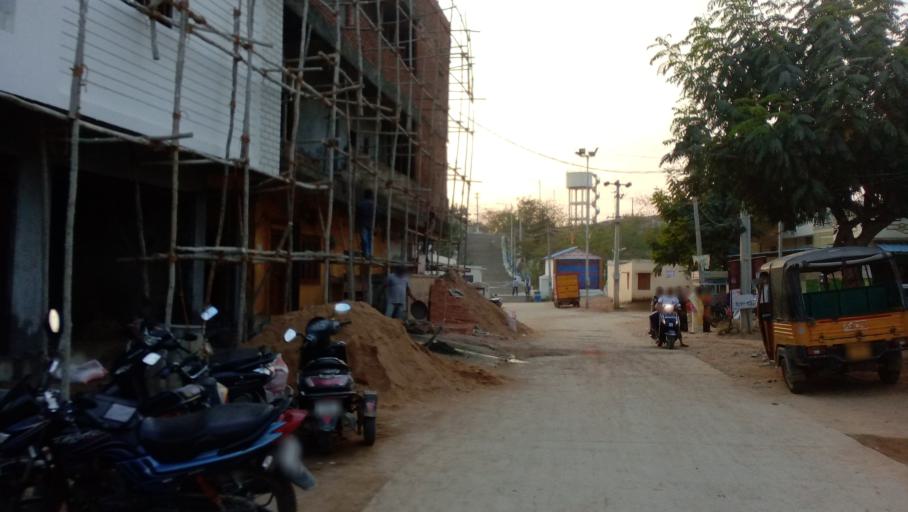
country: IN
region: Telangana
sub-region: Medak
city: Serilingampalle
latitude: 17.5186
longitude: 78.3090
